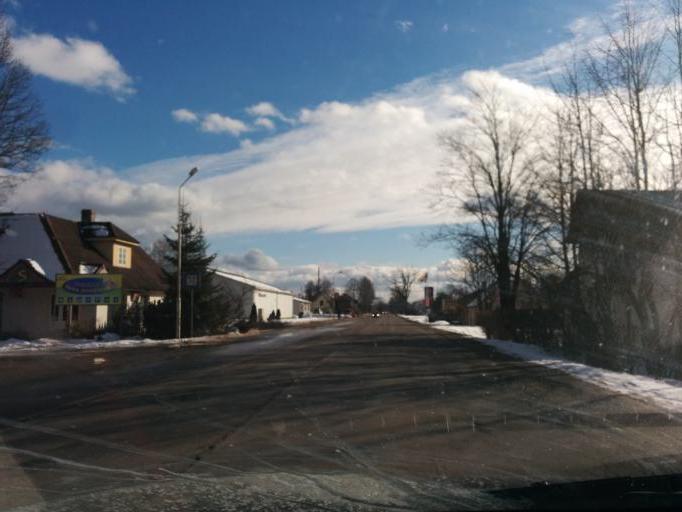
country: LV
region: Gulbenes Rajons
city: Gulbene
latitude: 57.1789
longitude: 26.7420
